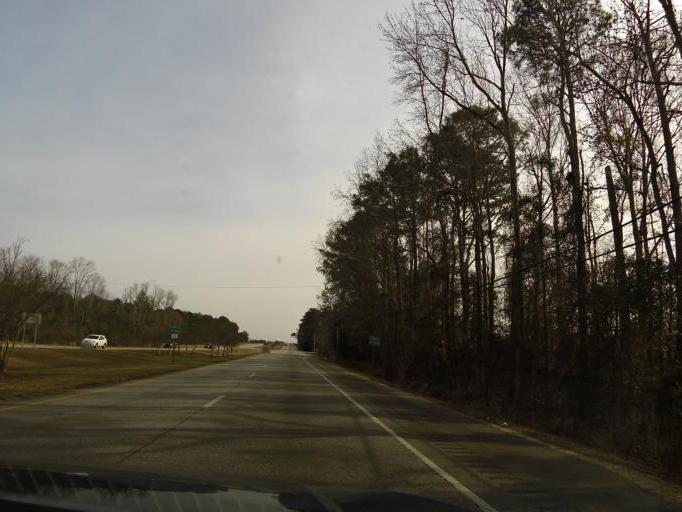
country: US
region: Alabama
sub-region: Houston County
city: Cowarts
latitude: 31.2000
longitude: -85.3399
